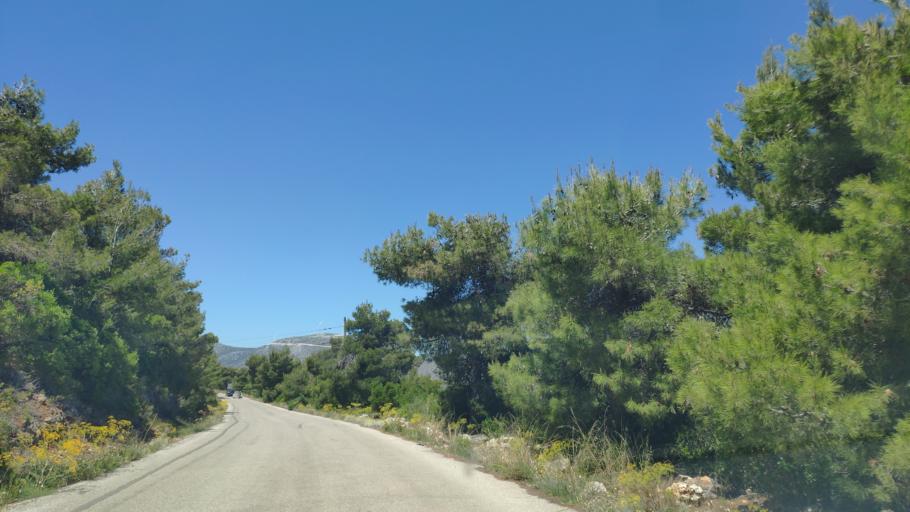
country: GR
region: Central Greece
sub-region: Nomos Voiotias
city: Kaparellion
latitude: 38.2015
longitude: 23.1575
